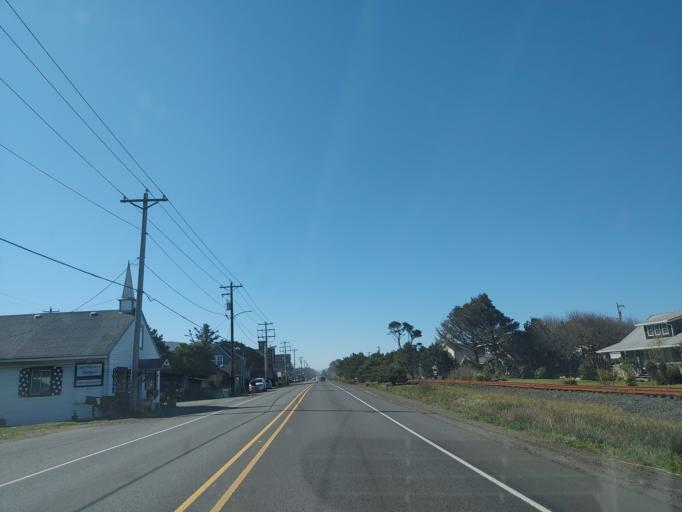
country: US
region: Oregon
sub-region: Tillamook County
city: Rockaway Beach
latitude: 45.6093
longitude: -123.9445
